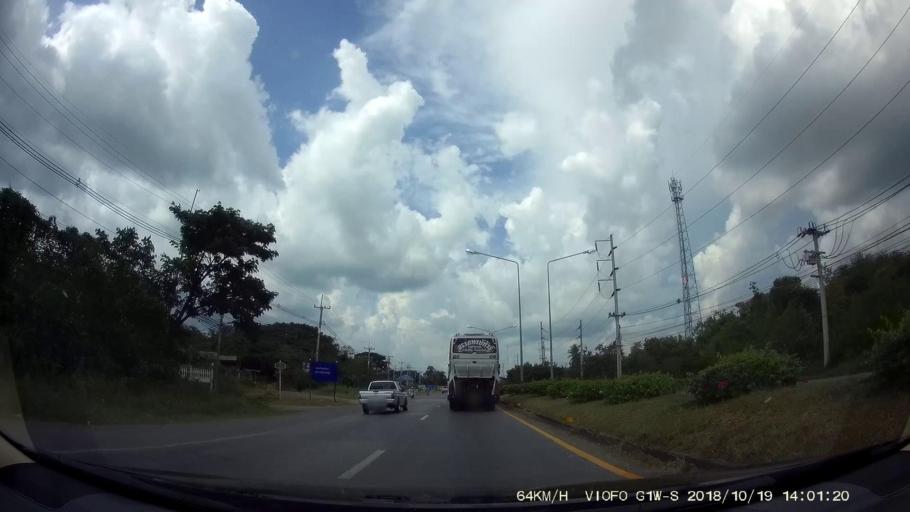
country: TH
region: Chaiyaphum
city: Chaiyaphum
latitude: 15.8283
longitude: 102.0588
